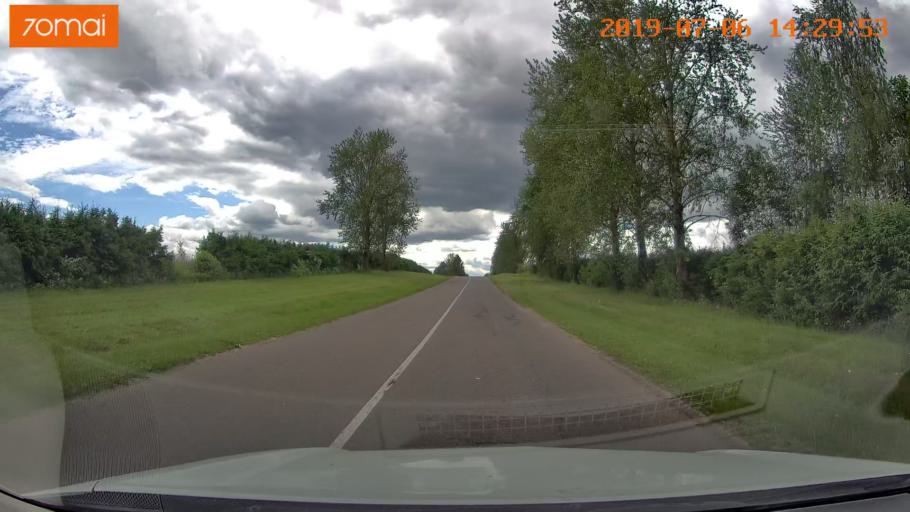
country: BY
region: Minsk
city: Ivyanyets
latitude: 53.9292
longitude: 26.7918
